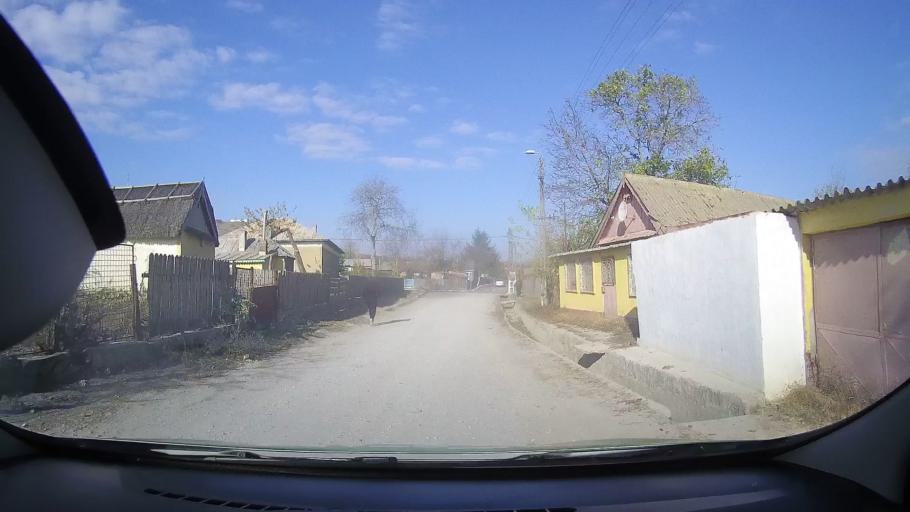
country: RO
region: Tulcea
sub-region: Comuna Mahmudia
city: Mahmudia
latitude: 45.0859
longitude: 29.0861
